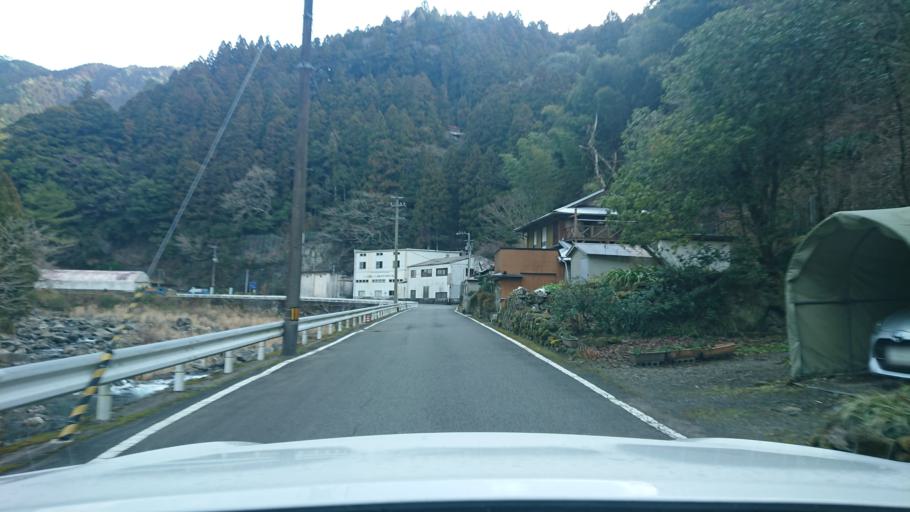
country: JP
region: Tokushima
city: Ishii
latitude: 33.8933
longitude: 134.4024
